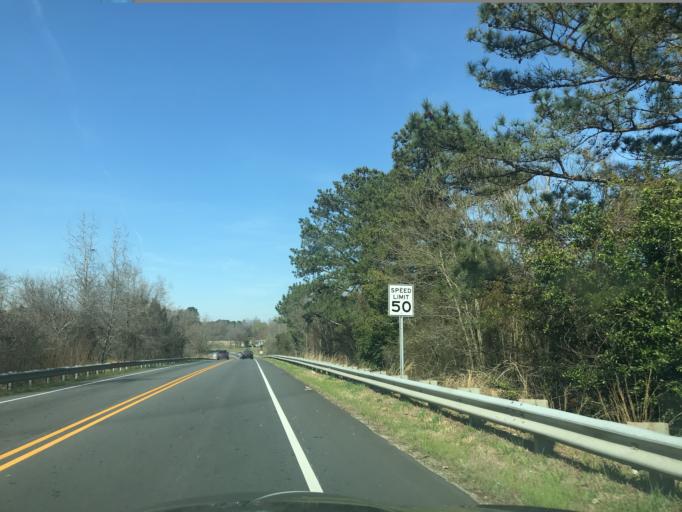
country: US
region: North Carolina
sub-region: Harnett County
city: Angier
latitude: 35.5551
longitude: -78.7557
